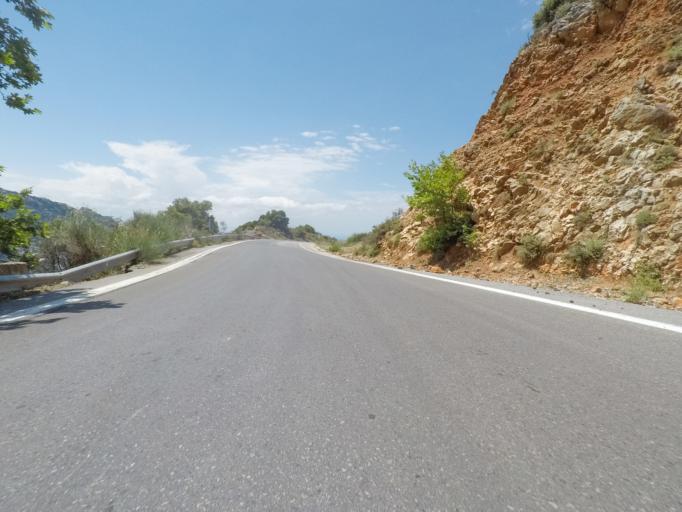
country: GR
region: Crete
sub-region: Nomos Irakleiou
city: Mokhos
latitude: 35.2139
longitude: 25.4618
